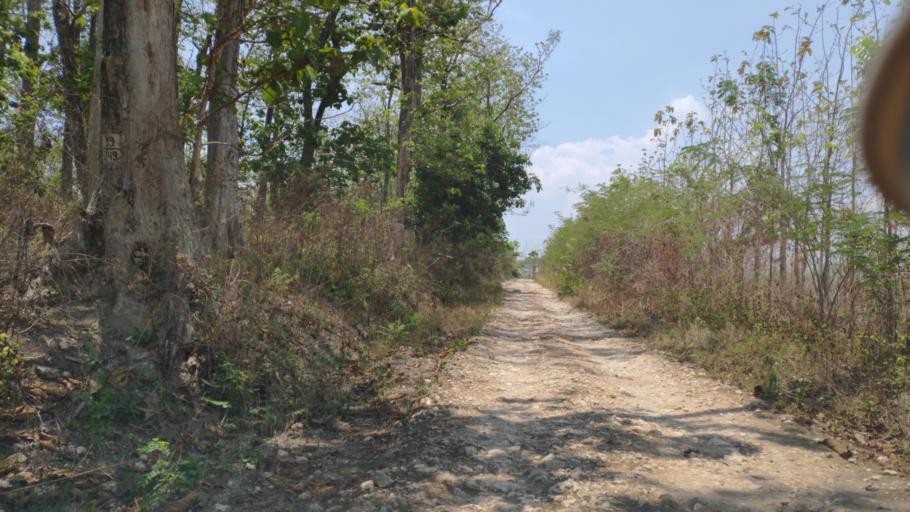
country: ID
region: Central Java
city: Botoh
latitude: -7.0736
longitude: 111.4807
